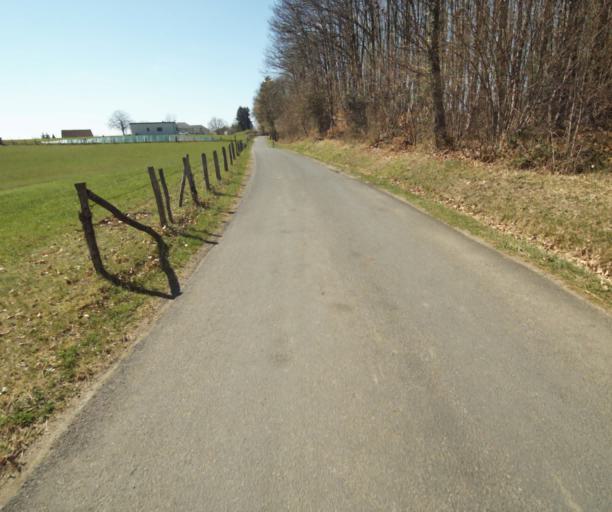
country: FR
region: Limousin
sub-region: Departement de la Correze
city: Saint-Clement
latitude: 45.3102
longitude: 1.6838
